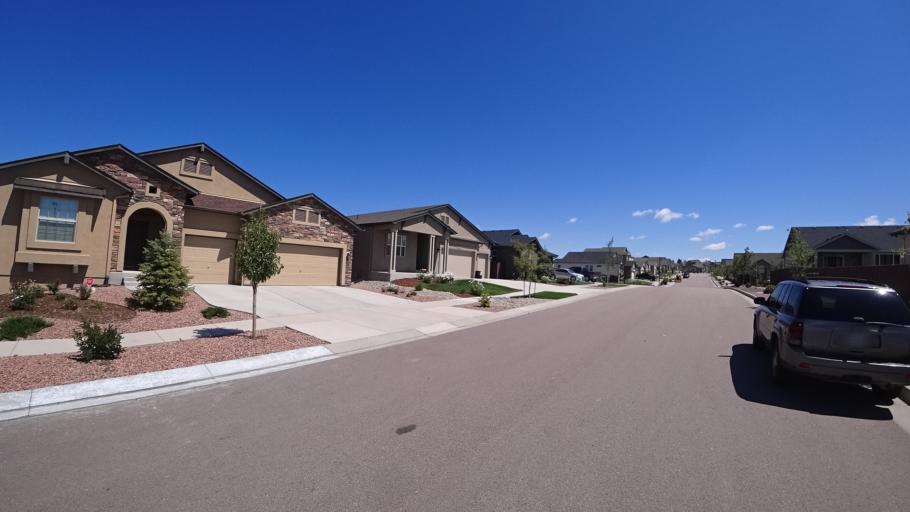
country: US
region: Colorado
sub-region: El Paso County
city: Black Forest
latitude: 38.9905
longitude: -104.7659
